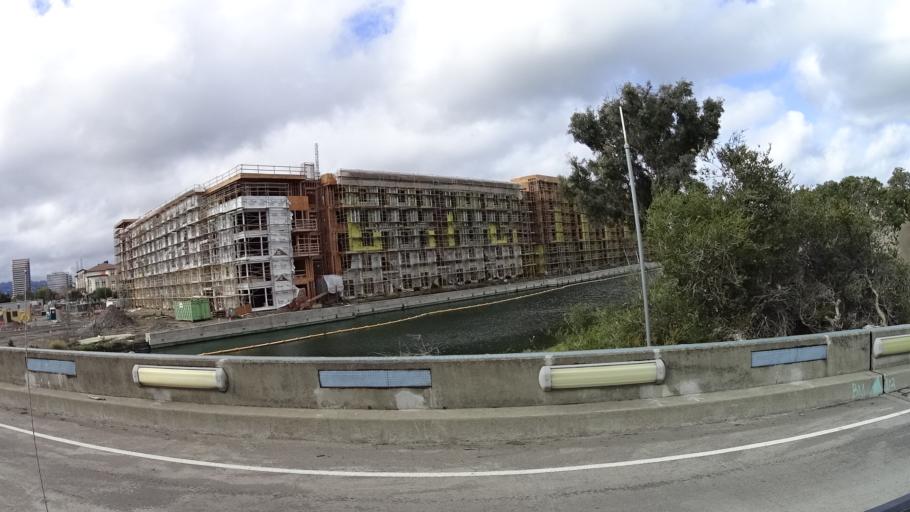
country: US
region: California
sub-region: San Mateo County
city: Foster City
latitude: 37.5658
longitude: -122.2680
